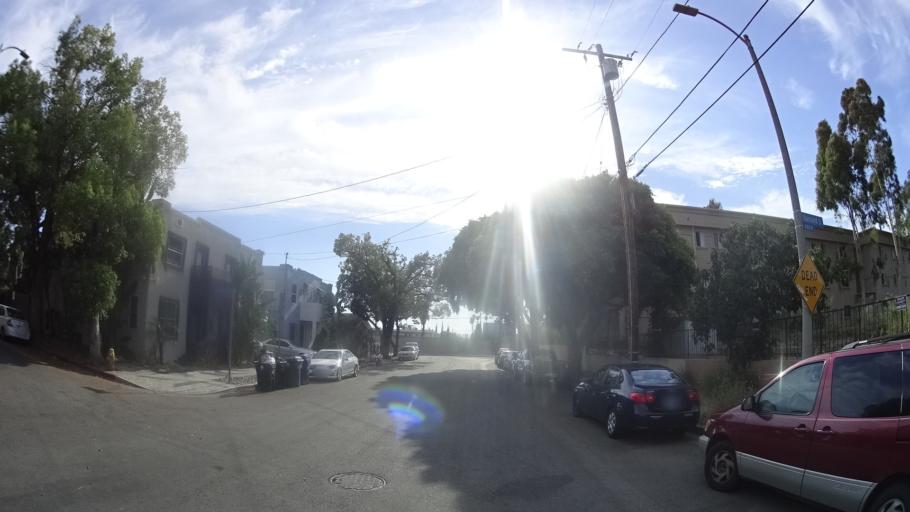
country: US
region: California
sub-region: Los Angeles County
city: Hollywood
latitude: 34.0885
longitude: -118.3039
